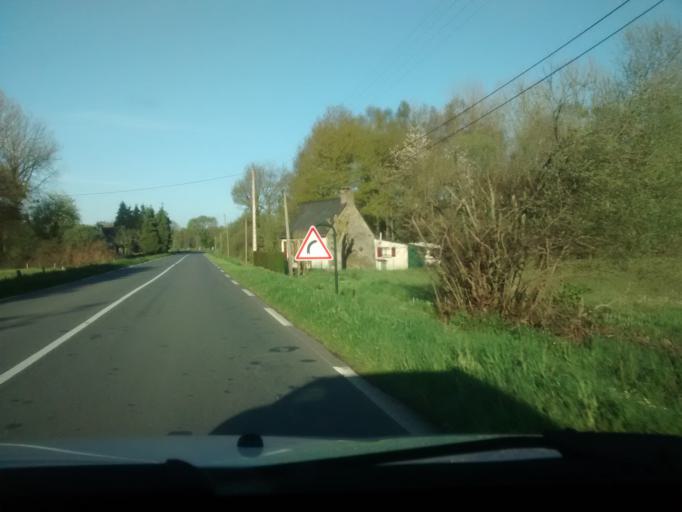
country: FR
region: Brittany
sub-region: Departement d'Ille-et-Vilaine
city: Antrain
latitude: 48.4680
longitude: -1.5188
